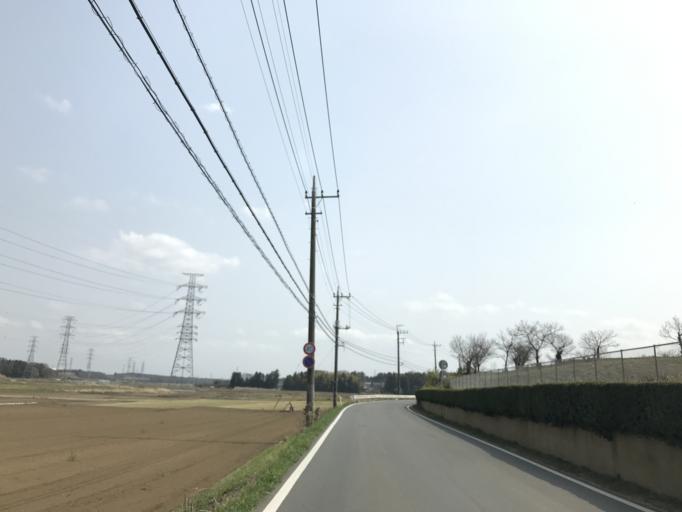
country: JP
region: Ibaraki
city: Ushiku
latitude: 36.0094
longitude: 140.0654
